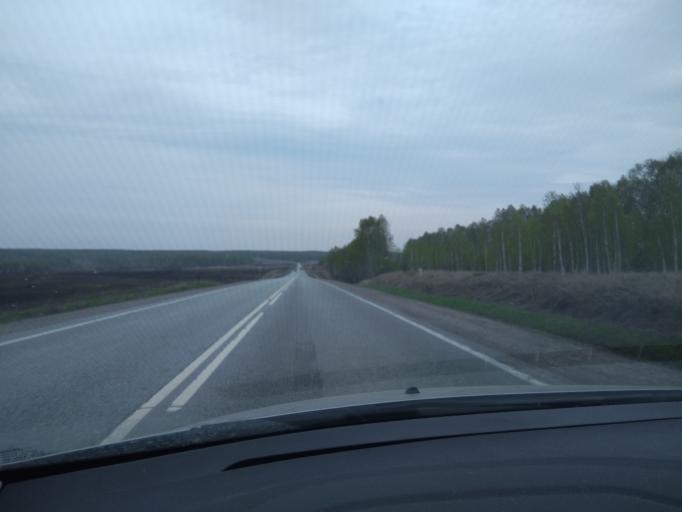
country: RU
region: Sverdlovsk
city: Yelanskiy
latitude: 56.7590
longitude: 62.3654
